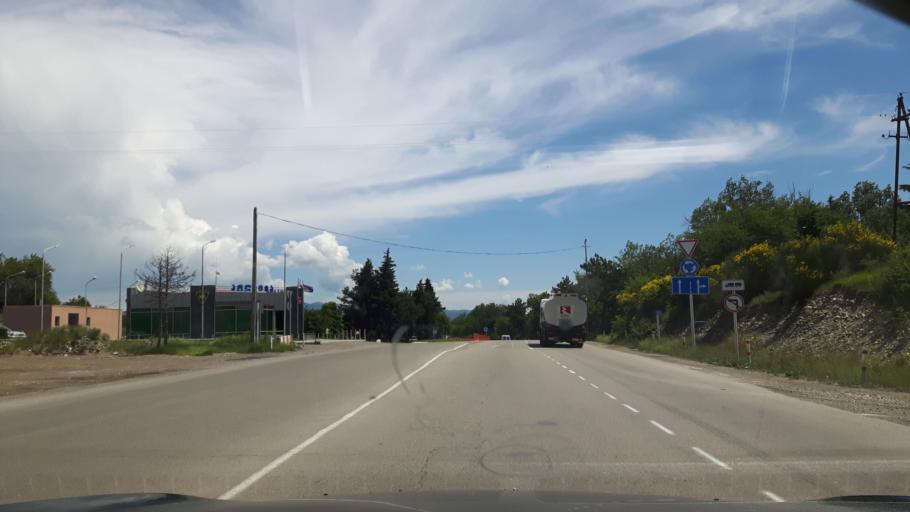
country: GE
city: Didi Lilo
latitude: 41.6955
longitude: 45.0931
